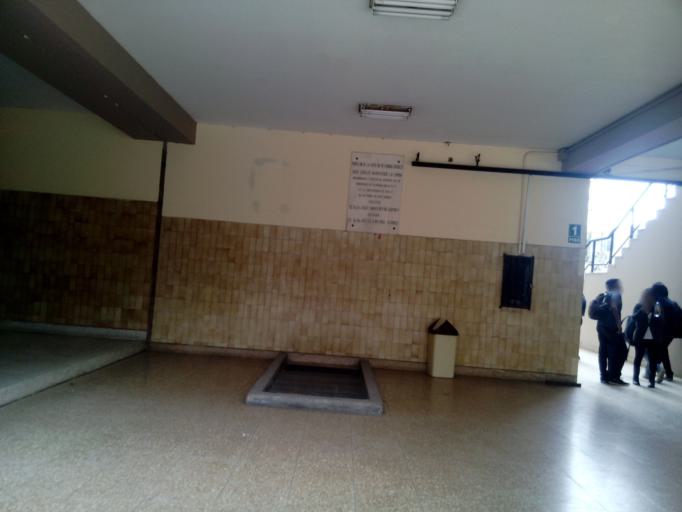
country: PE
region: Callao
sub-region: Callao
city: Callao
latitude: -12.0583
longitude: -77.0815
